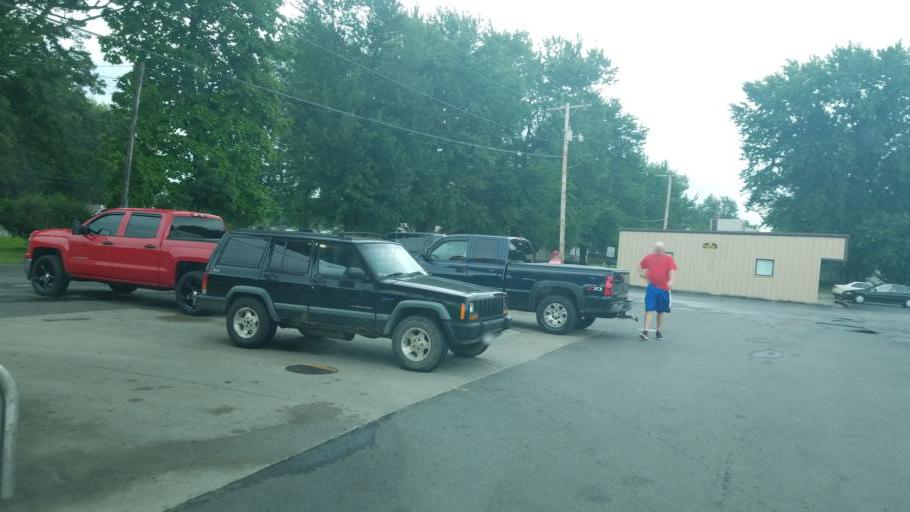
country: US
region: Ohio
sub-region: Logan County
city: Russells Point
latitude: 40.5203
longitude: -83.8877
